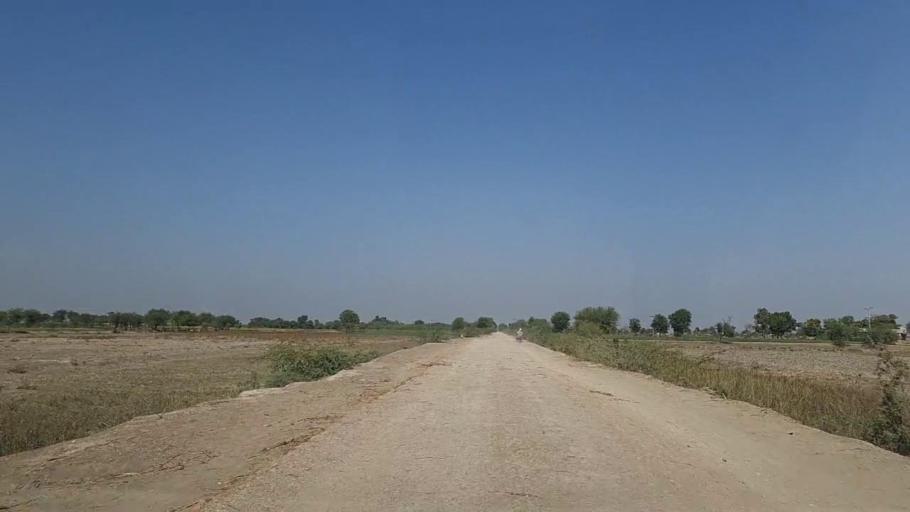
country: PK
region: Sindh
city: Samaro
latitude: 25.1761
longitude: 69.4040
